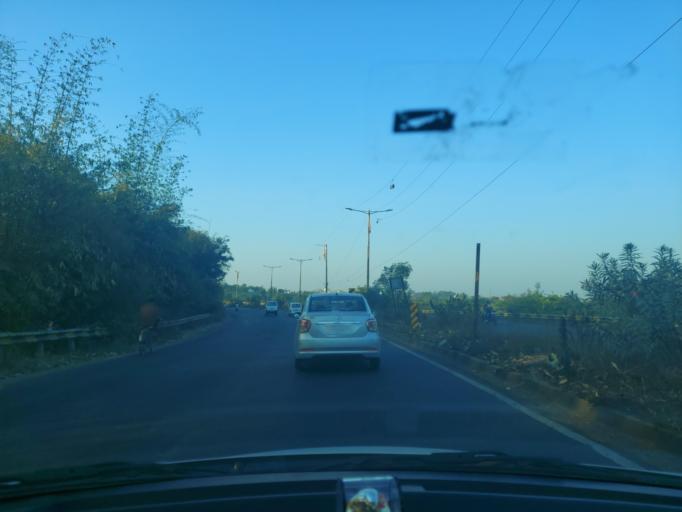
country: IN
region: Madhya Pradesh
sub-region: Ujjain
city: Ujjain
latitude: 23.1313
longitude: 75.7959
